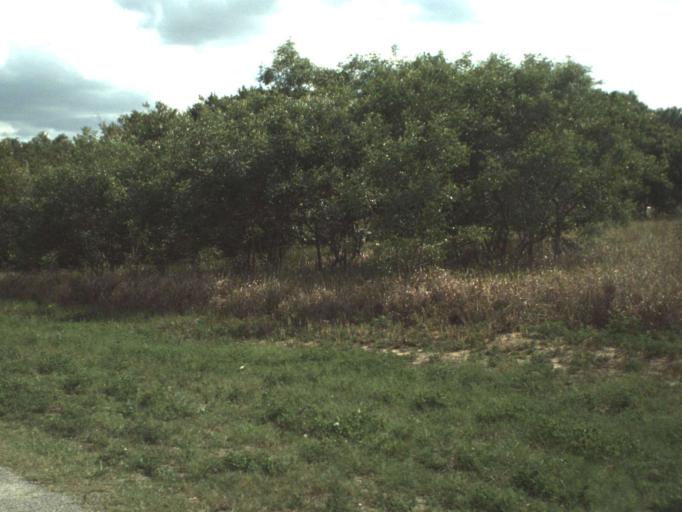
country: US
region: Florida
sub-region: Marion County
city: Silver Springs Shores
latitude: 29.0944
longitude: -82.0536
